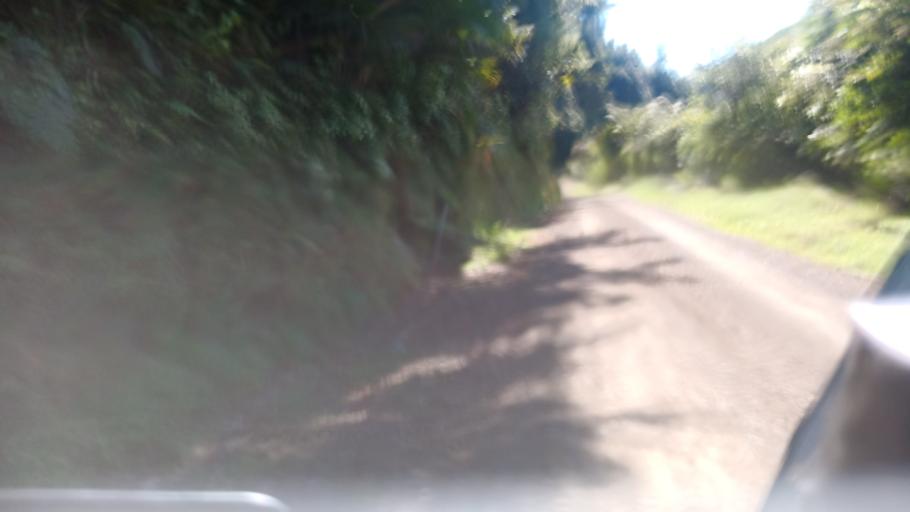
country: NZ
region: Bay of Plenty
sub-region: Opotiki District
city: Opotiki
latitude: -38.0742
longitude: 177.4734
